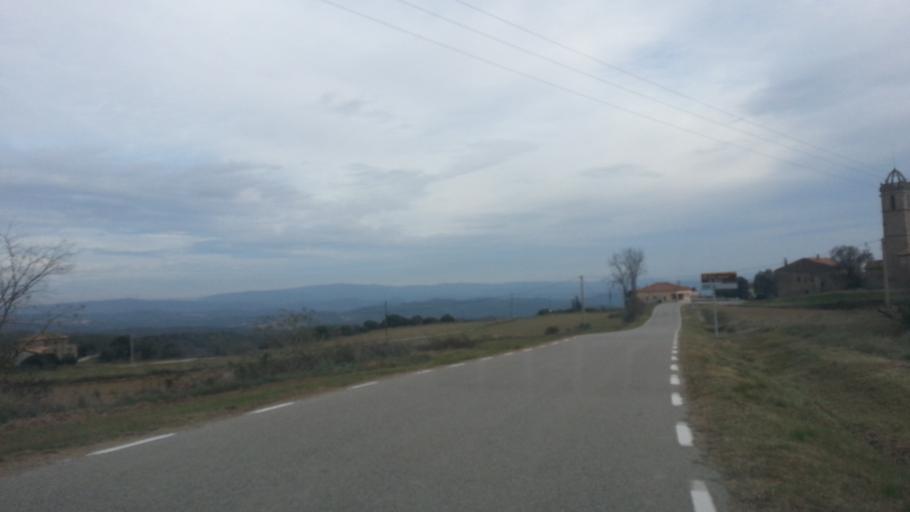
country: ES
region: Catalonia
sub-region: Provincia de Barcelona
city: Puig-reig
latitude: 41.9570
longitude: 1.8111
